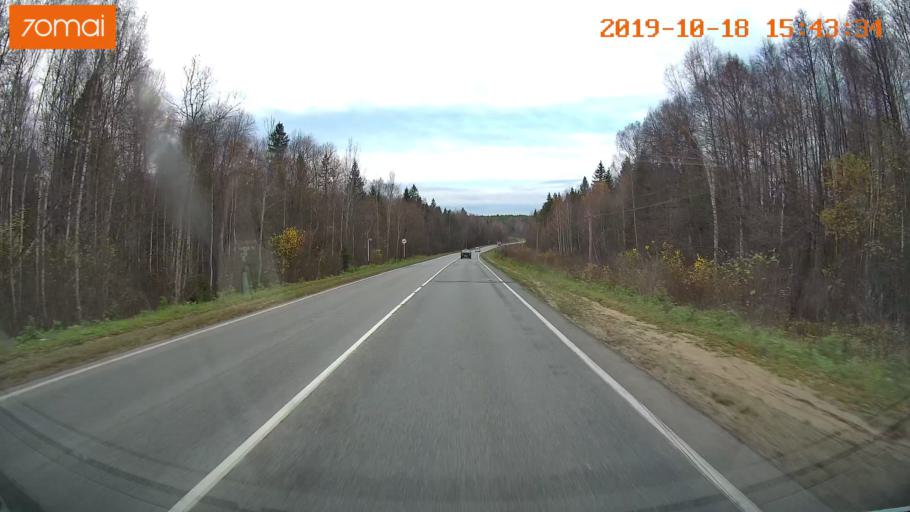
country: RU
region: Vladimir
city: Golovino
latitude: 55.9695
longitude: 40.5495
